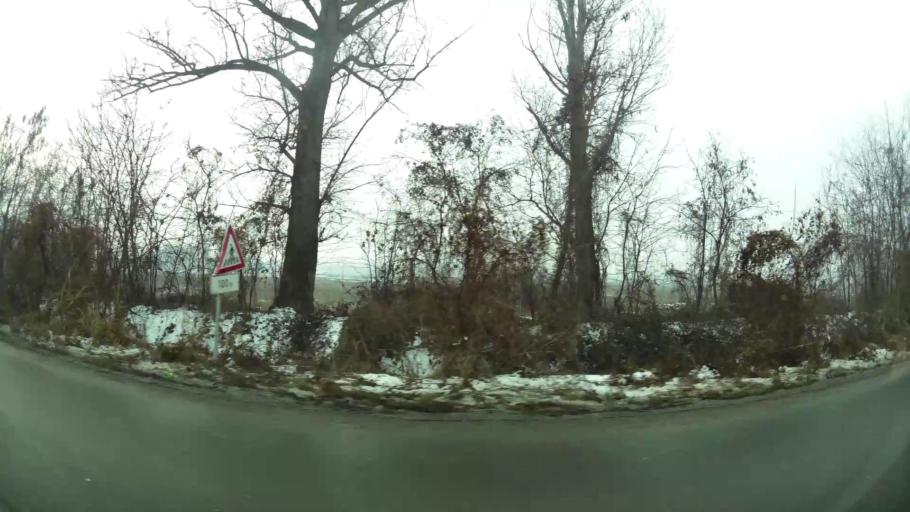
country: MK
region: Ilinden
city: Idrizovo
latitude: 41.9540
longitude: 21.5780
